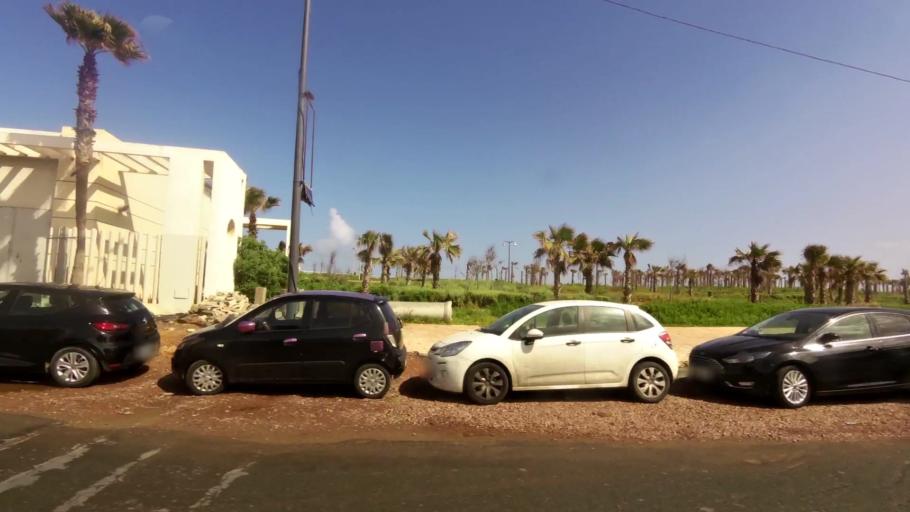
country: MA
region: Grand Casablanca
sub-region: Casablanca
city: Casablanca
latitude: 33.6089
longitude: -7.6277
